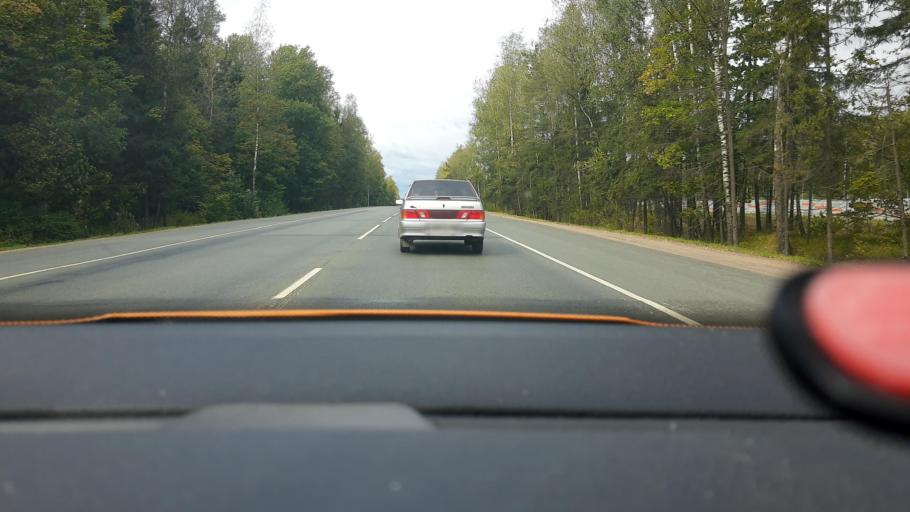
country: RU
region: Moskovskaya
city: Zelenogradskiy
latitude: 56.0942
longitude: 37.9821
